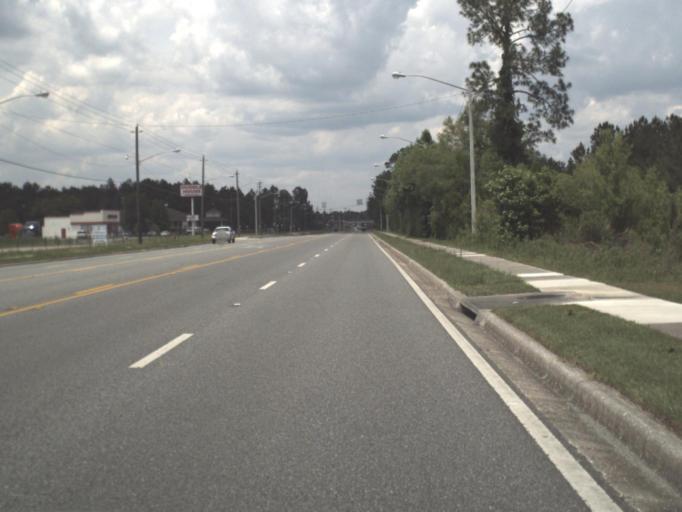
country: US
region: Florida
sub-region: Columbia County
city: Five Points
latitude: 30.2341
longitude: -82.6385
